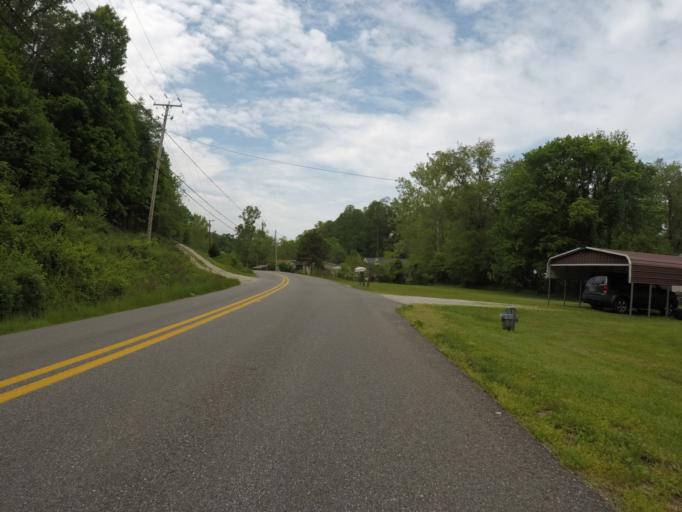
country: US
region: West Virginia
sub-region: Wayne County
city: Ceredo
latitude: 38.3544
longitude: -82.5599
